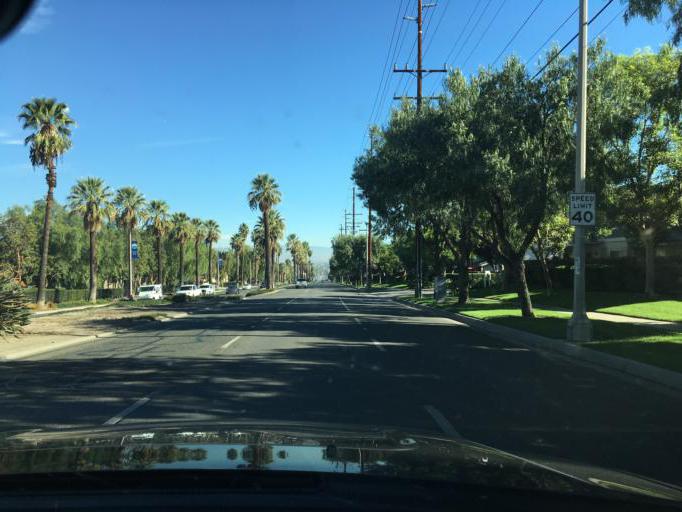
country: US
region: California
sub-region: Riverside County
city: Corona
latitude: 33.8615
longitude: -117.5497
